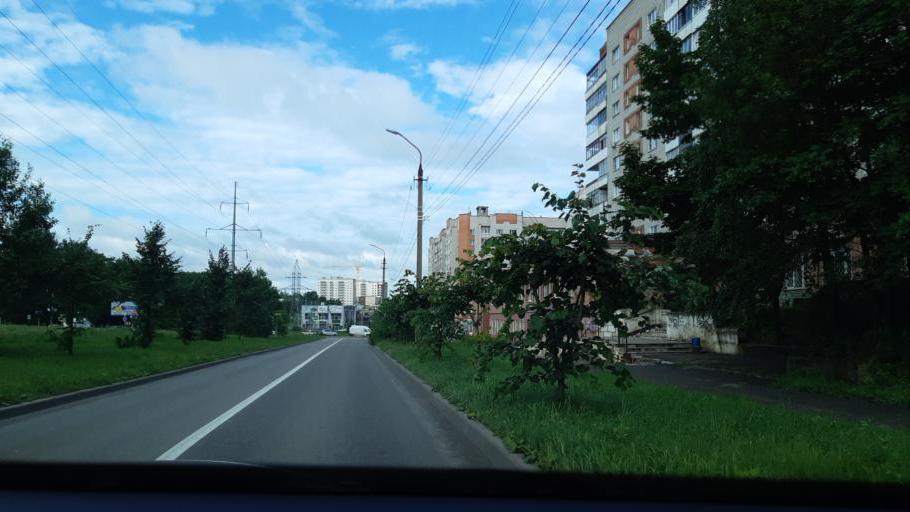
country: RU
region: Smolensk
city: Smolensk
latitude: 54.7620
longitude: 32.0857
